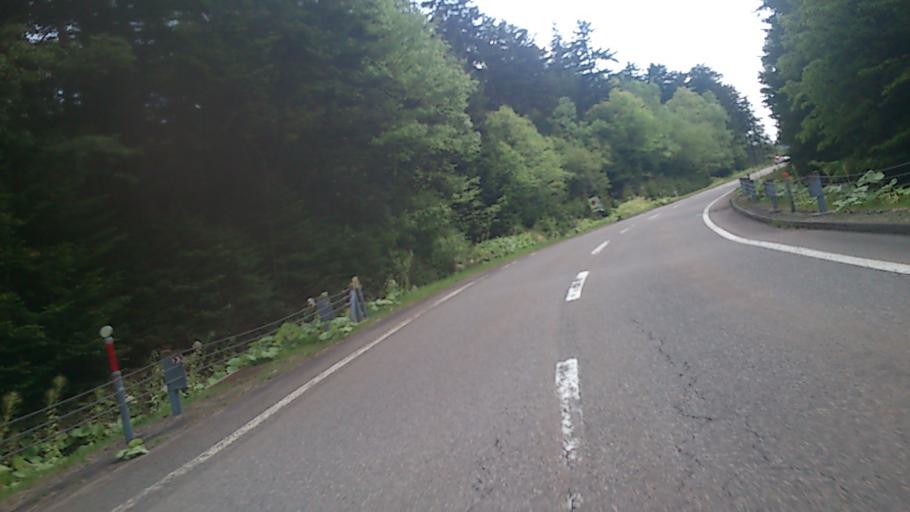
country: JP
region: Hokkaido
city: Kitami
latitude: 43.3982
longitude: 143.9868
